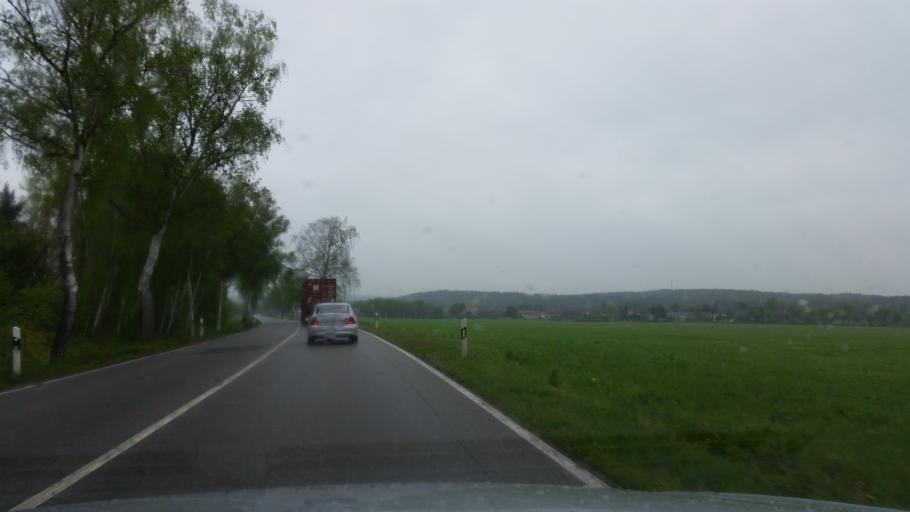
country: DE
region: Saxony-Anhalt
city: Kalbe
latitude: 52.5927
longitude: 11.3408
